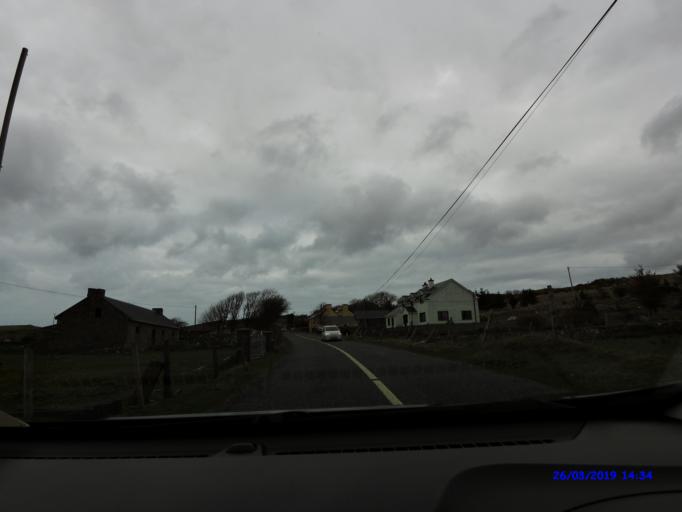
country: IE
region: Connaught
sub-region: Maigh Eo
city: Crossmolina
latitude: 54.2949
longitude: -9.5485
